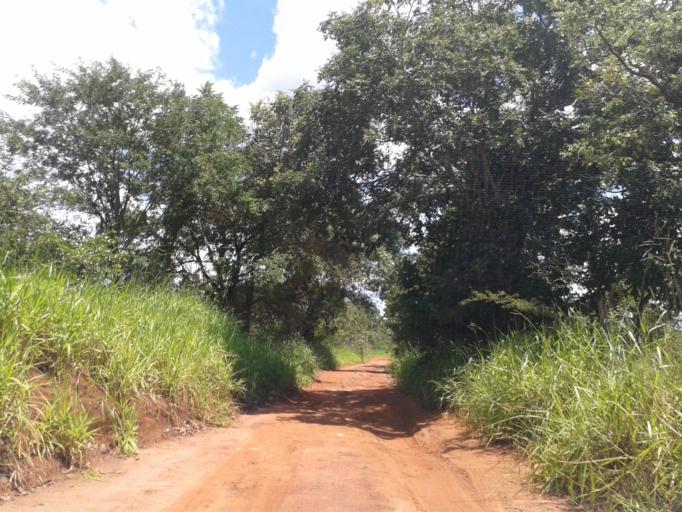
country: BR
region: Minas Gerais
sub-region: Ituiutaba
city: Ituiutaba
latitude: -18.8517
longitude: -49.5009
